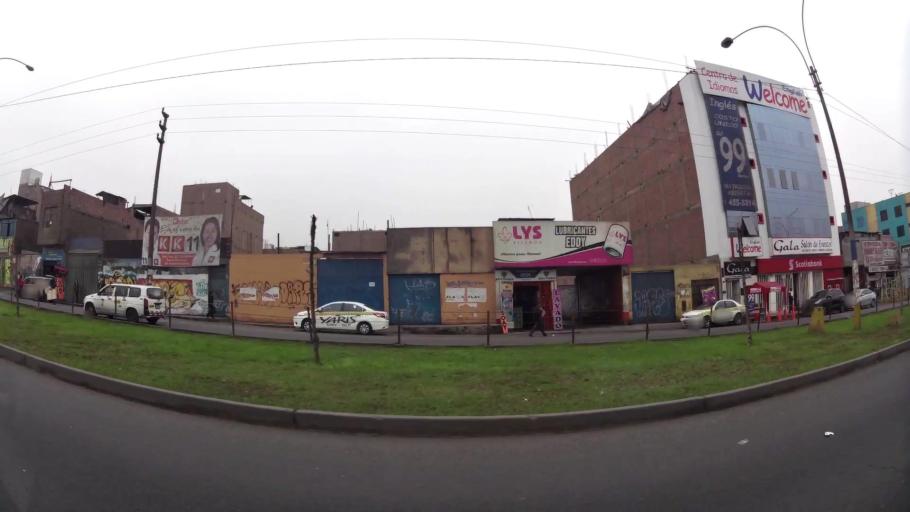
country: PE
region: Lima
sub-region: Lima
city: Independencia
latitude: -11.9498
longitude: -76.9865
